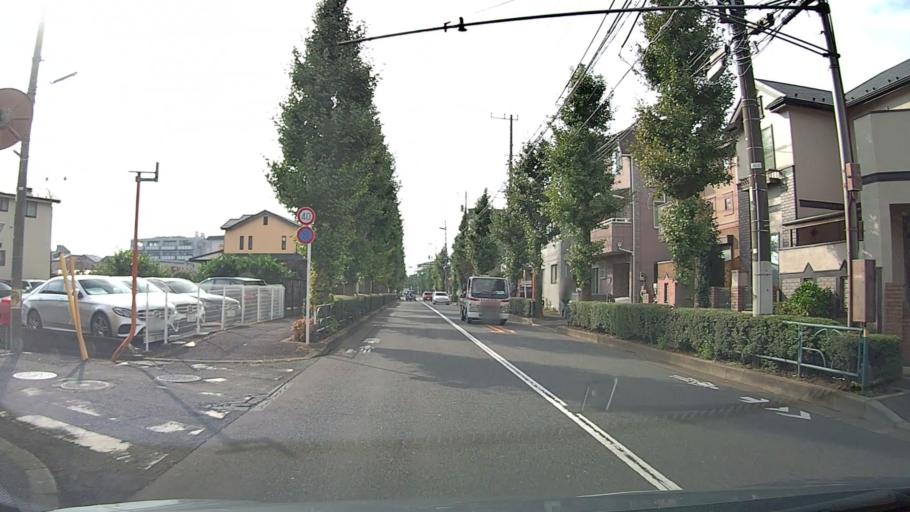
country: JP
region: Tokyo
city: Musashino
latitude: 35.7337
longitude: 139.5681
